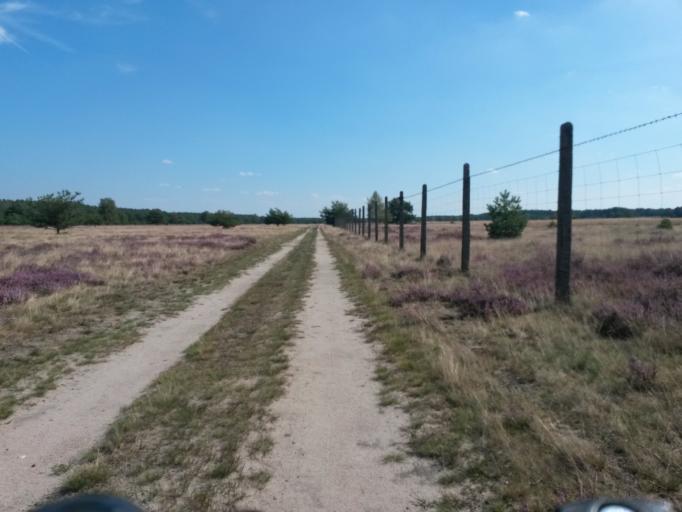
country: DE
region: Brandenburg
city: Templin
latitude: 53.0331
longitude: 13.5566
